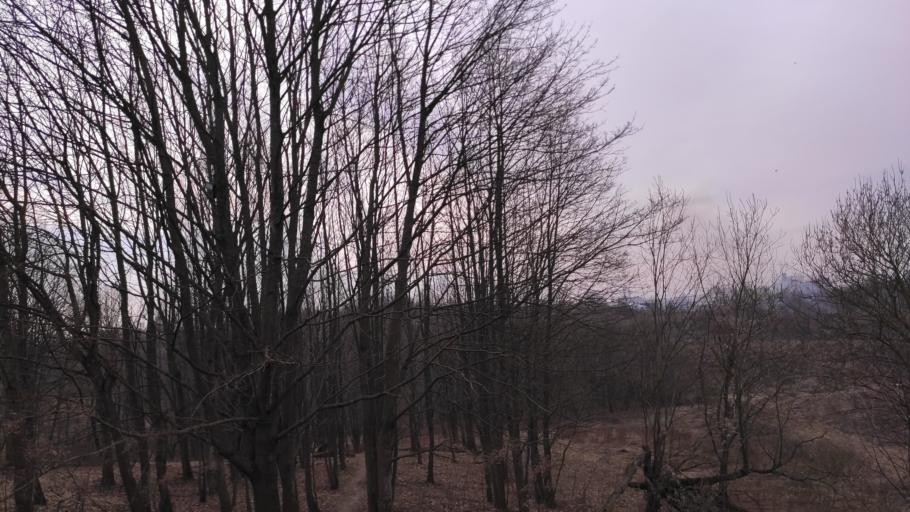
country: BY
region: Minsk
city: Novoye Medvezhino
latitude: 53.8874
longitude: 27.4679
